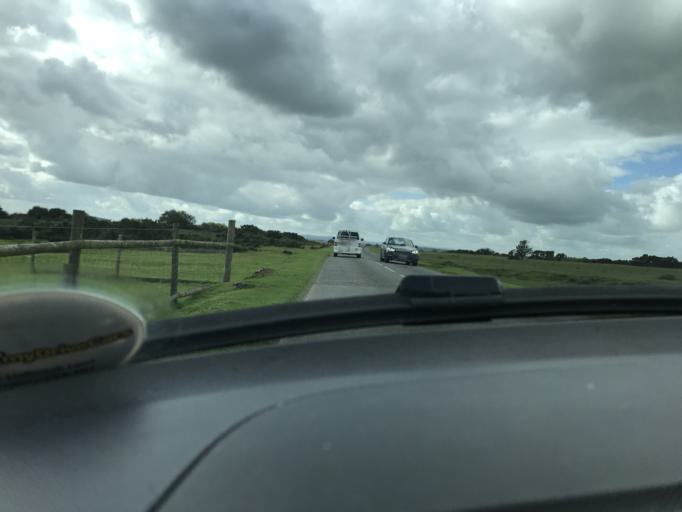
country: GB
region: England
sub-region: Devon
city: Horrabridge
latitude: 50.5423
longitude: -4.1040
